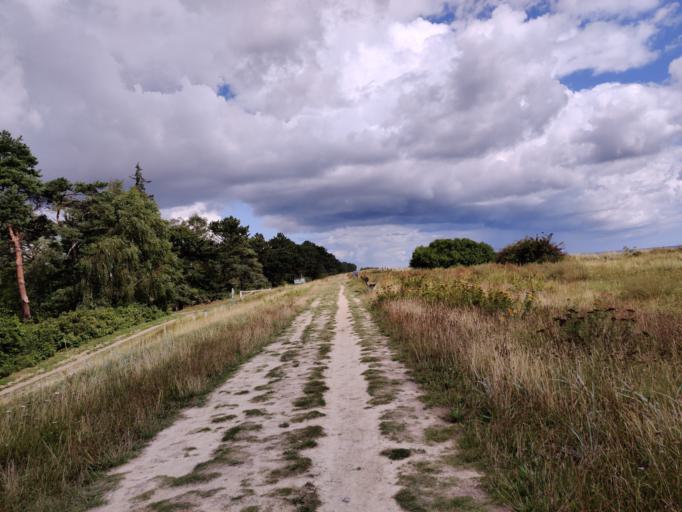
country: DK
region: Zealand
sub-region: Guldborgsund Kommune
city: Nykobing Falster
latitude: 54.7106
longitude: 11.9904
